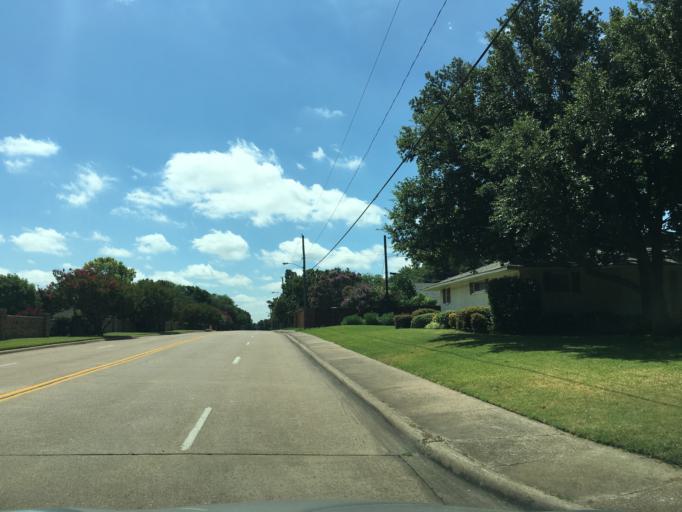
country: US
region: Texas
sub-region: Dallas County
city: Garland
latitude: 32.8396
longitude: -96.6506
